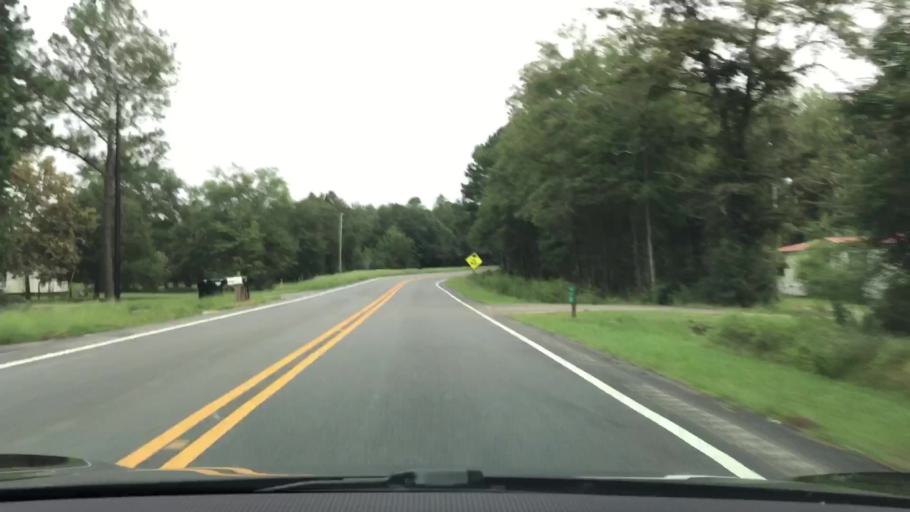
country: US
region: Alabama
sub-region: Covington County
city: Opp
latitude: 31.2263
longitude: -86.1614
